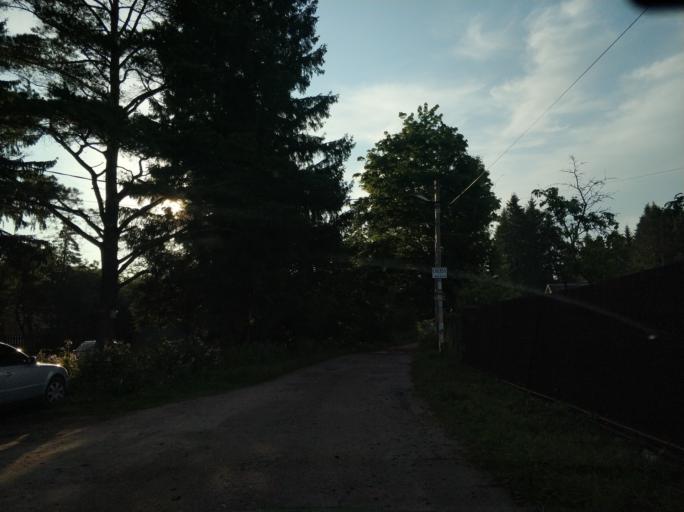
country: RU
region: Leningrad
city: Shcheglovo
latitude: 60.0525
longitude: 30.7472
